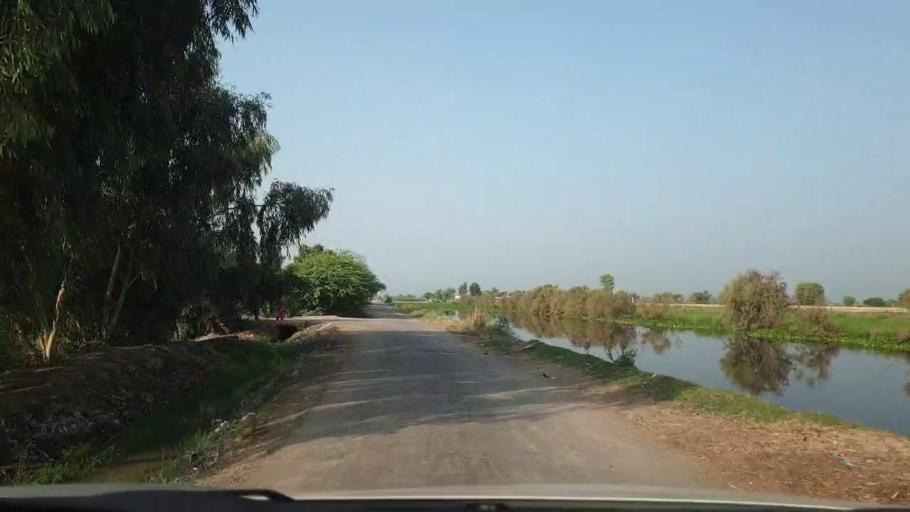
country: PK
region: Sindh
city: Larkana
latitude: 27.5055
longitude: 68.1793
